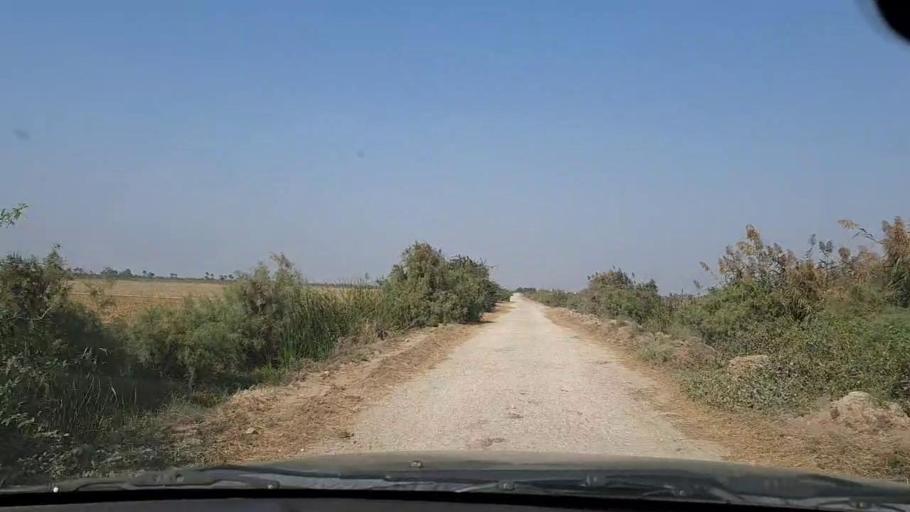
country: PK
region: Sindh
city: Mirpur Sakro
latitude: 24.3529
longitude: 67.6831
